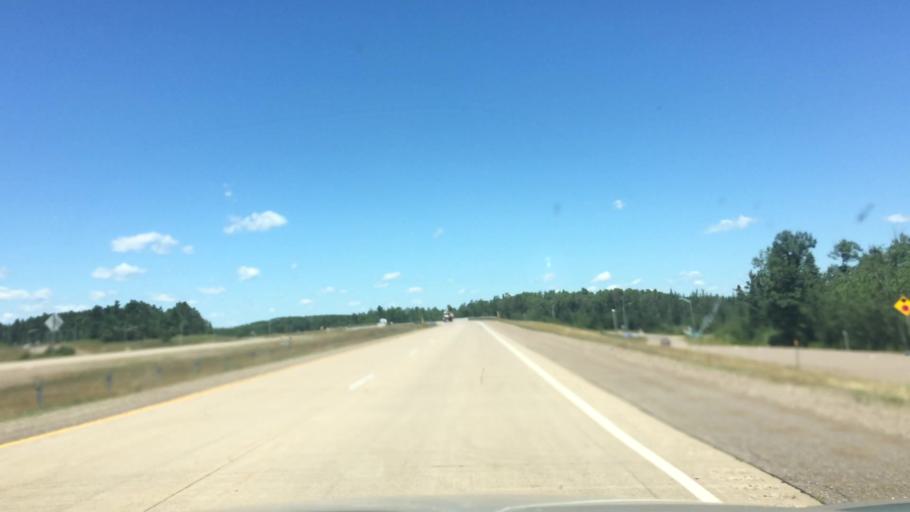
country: US
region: Wisconsin
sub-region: Lincoln County
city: Tomahawk
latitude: 45.4144
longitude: -89.6712
